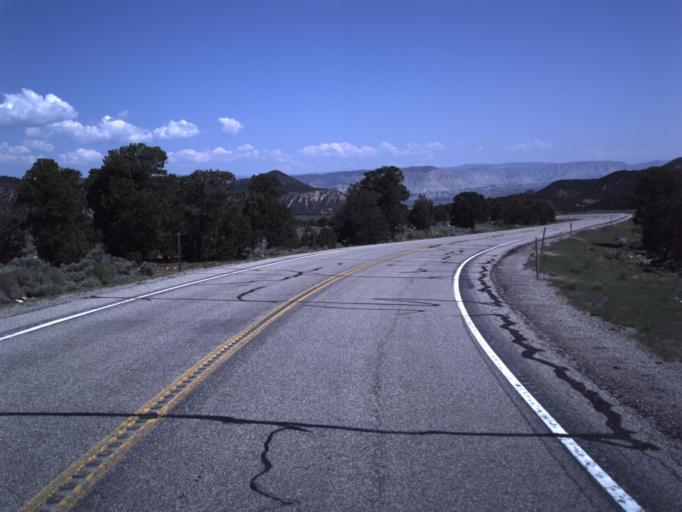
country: US
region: Utah
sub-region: Wayne County
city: Loa
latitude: 38.7040
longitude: -111.4023
